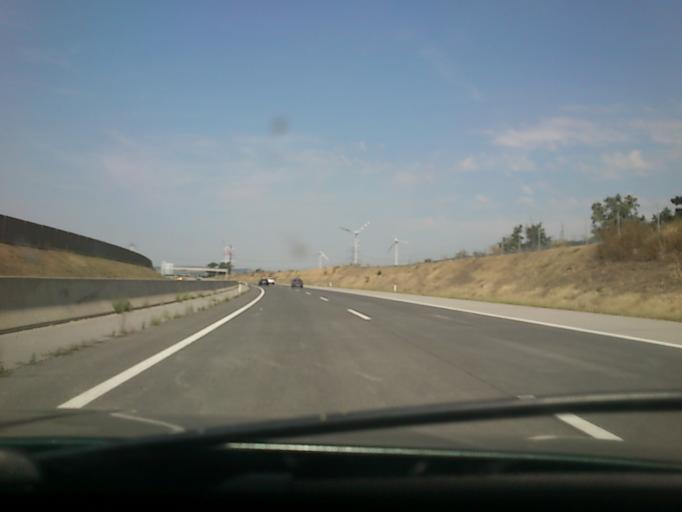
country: AT
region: Lower Austria
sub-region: Politischer Bezirk Mistelbach
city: Pillichsdorf
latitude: 48.3338
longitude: 16.5133
